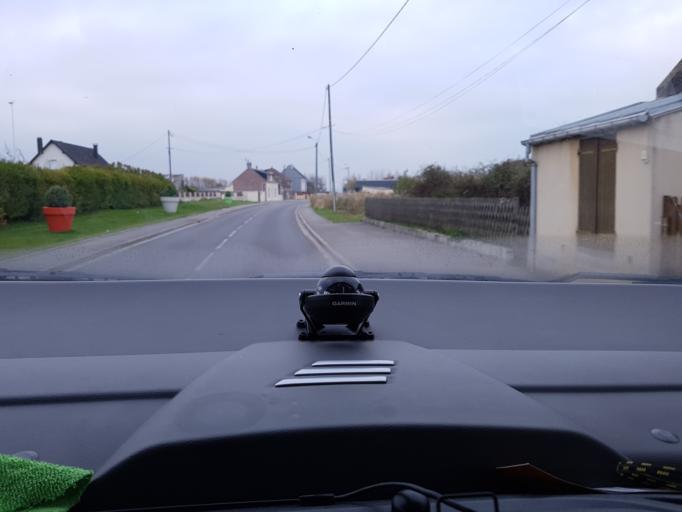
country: FR
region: Picardie
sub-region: Departement de la Somme
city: Cayeux-sur-Mer
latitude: 50.1698
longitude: 1.4949
